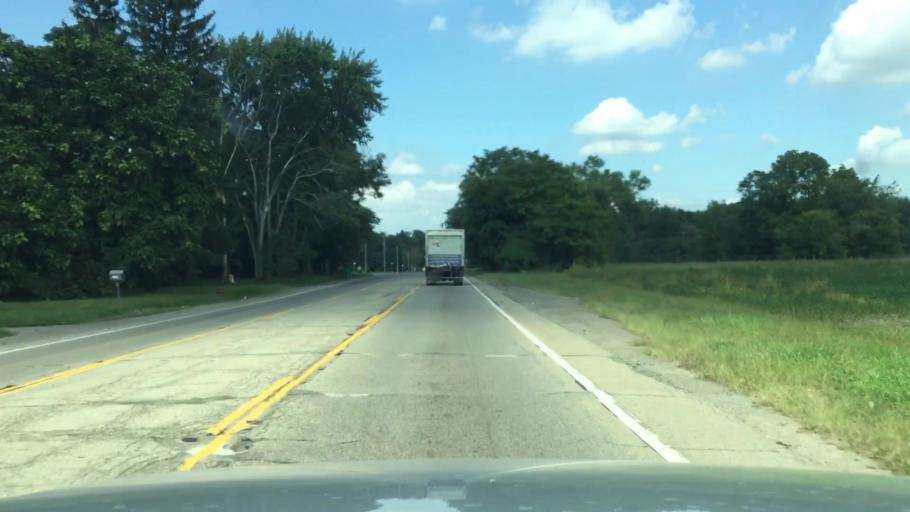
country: US
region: Michigan
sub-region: Wayne County
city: Romulus
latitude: 42.2462
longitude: -83.3862
